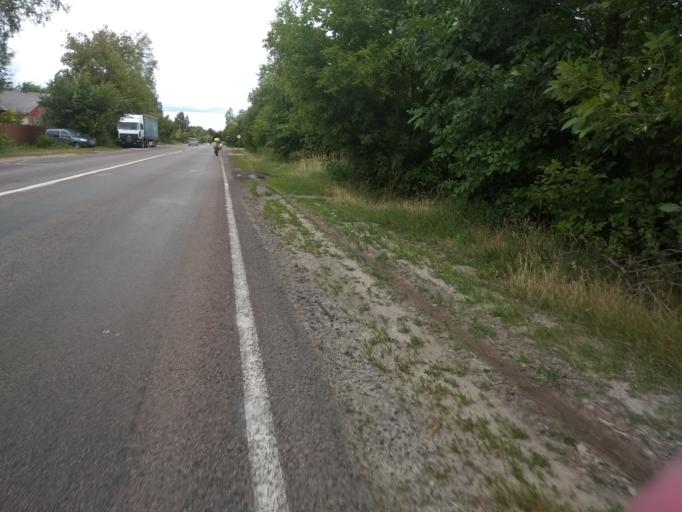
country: RU
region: Moskovskaya
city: Misheronskiy
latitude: 55.5976
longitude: 39.7040
